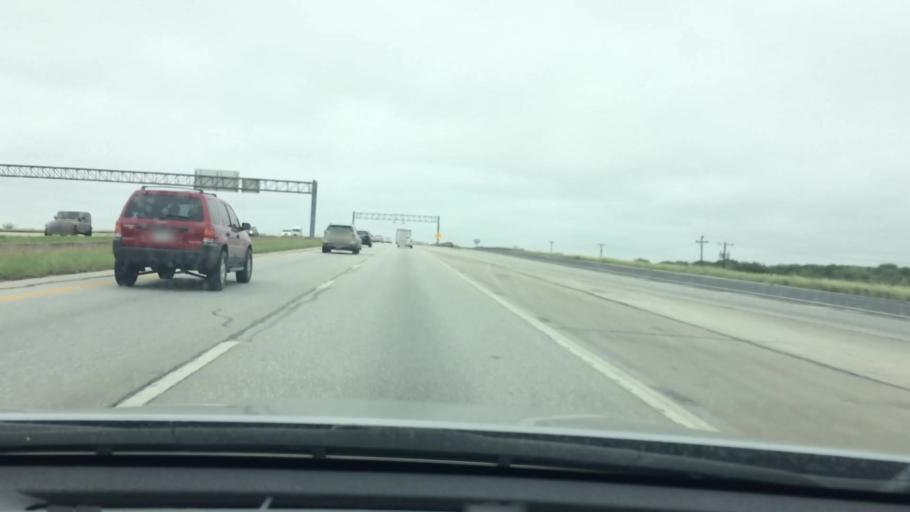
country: US
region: Texas
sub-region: Bexar County
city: Live Oak
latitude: 29.5835
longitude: -98.3464
